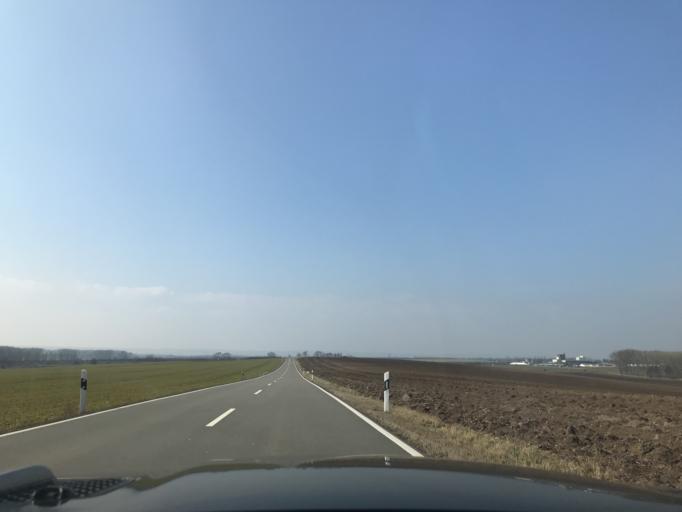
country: DE
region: Thuringia
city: Grossengottern
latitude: 51.1345
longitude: 10.5828
